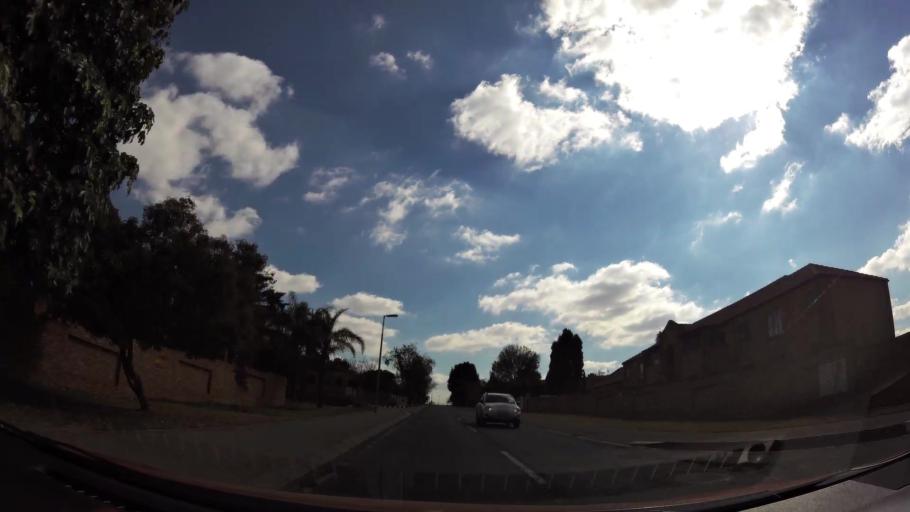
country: ZA
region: Gauteng
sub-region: City of Johannesburg Metropolitan Municipality
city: Roodepoort
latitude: -26.0843
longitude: 27.9359
